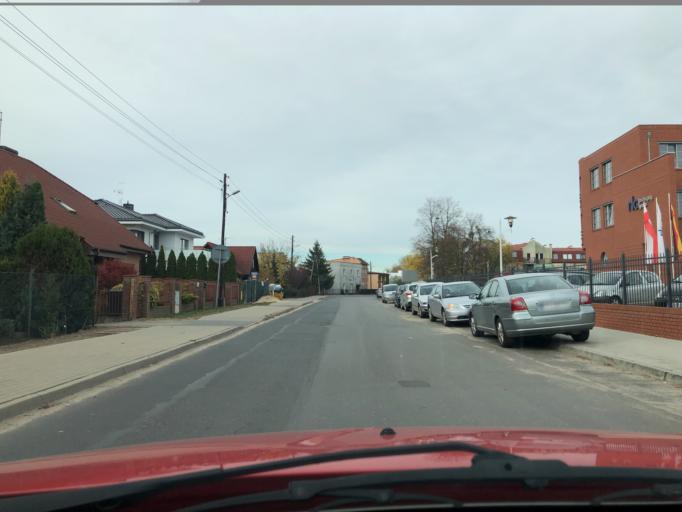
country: PL
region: Greater Poland Voivodeship
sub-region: Powiat poznanski
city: Plewiska
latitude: 52.3801
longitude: 16.8369
